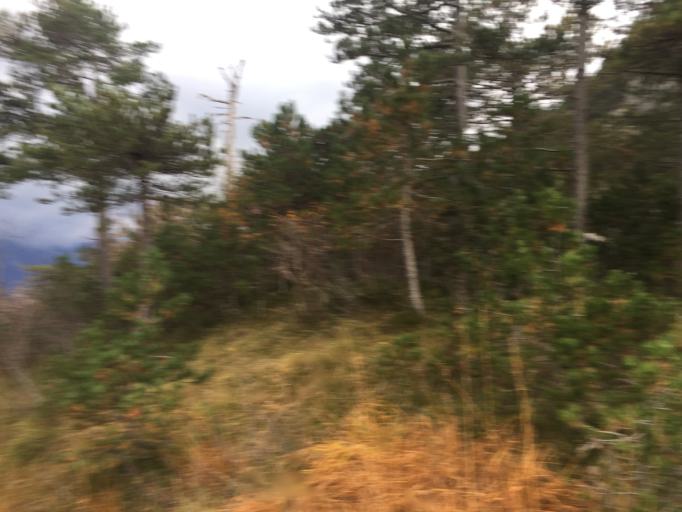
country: IT
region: Friuli Venezia Giulia
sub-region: Provincia di Udine
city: Chiusaforte
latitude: 46.4189
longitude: 13.3073
